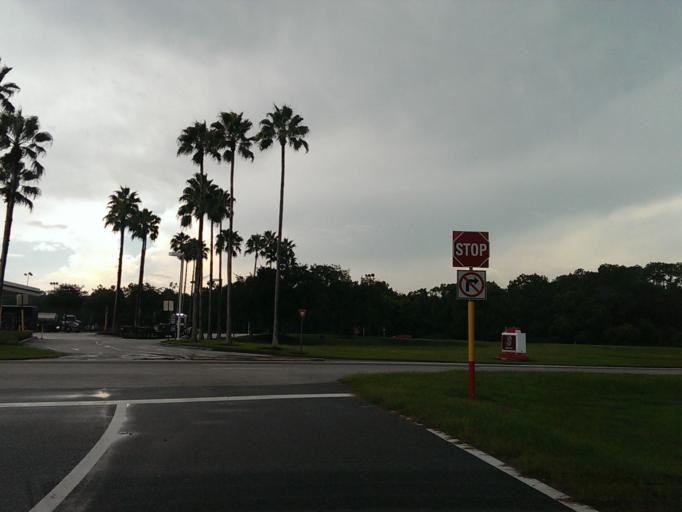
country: US
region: Florida
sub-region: Osceola County
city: Celebration
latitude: 28.3943
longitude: -81.5752
